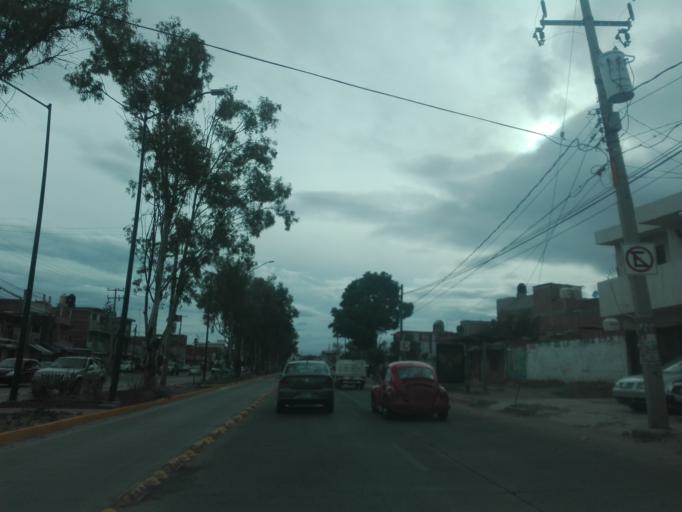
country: MX
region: Guanajuato
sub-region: Leon
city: Medina
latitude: 21.1418
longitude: -101.6384
